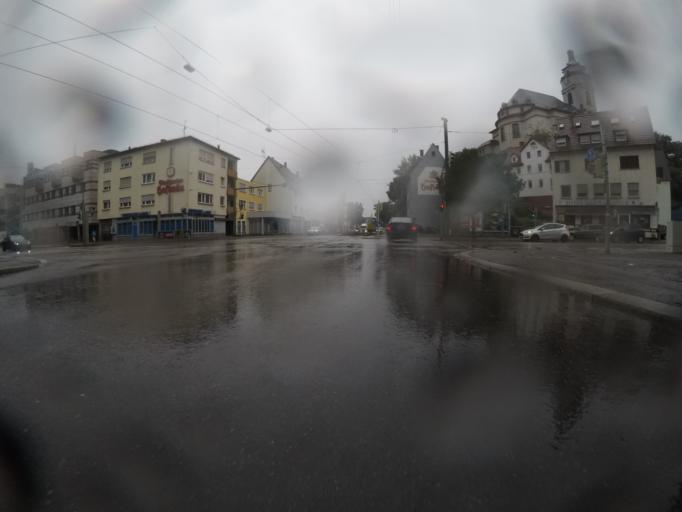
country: DE
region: Baden-Wuerttemberg
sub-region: Regierungsbezirk Stuttgart
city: Stuttgart-Ost
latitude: 48.7869
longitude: 9.2178
